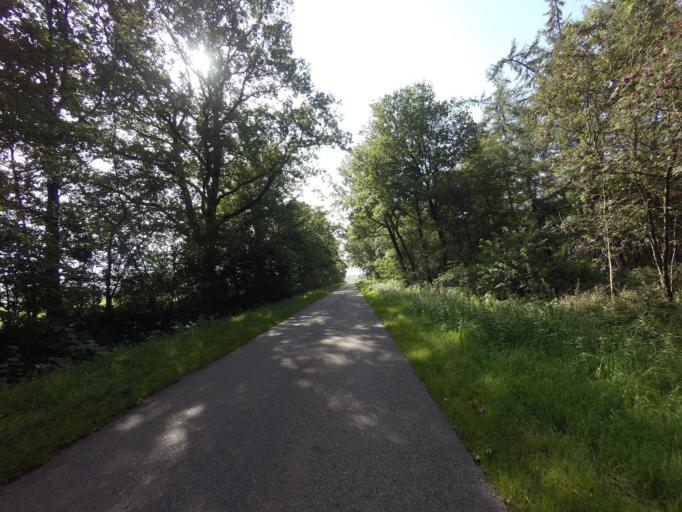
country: NL
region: Drenthe
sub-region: Gemeente Borger-Odoorn
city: Borger
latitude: 52.9364
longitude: 6.6975
